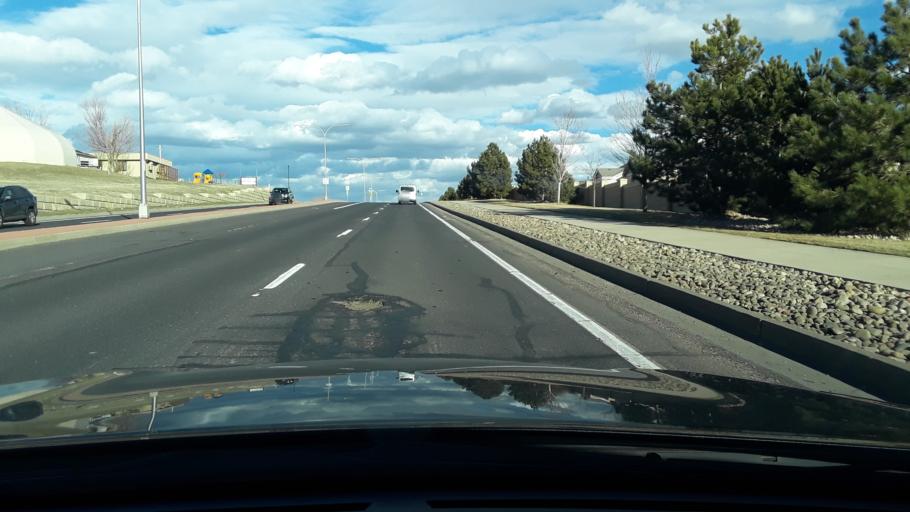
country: US
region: Colorado
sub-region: El Paso County
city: Gleneagle
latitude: 39.0272
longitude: -104.8123
